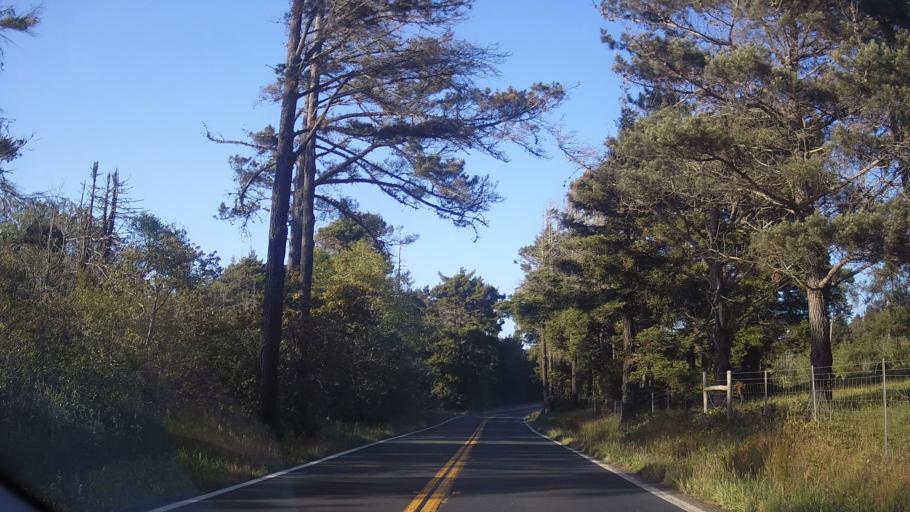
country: US
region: California
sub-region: Mendocino County
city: Fort Bragg
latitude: 39.5010
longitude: -123.7734
